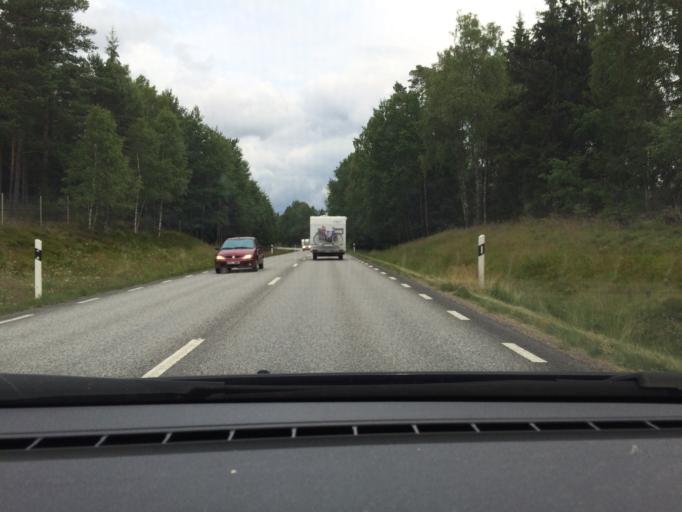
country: SE
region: Joenkoeping
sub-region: Varnamo Kommun
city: Forsheda
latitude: 57.1625
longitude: 13.8631
